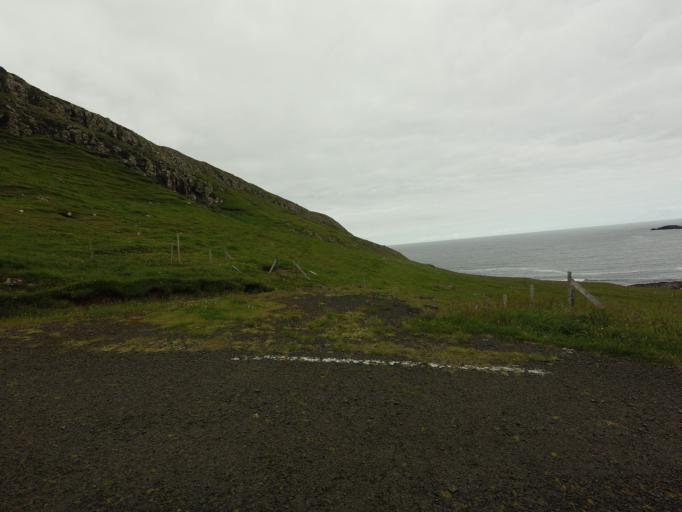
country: FO
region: Suduroy
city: Vagur
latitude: 61.4429
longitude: -6.7272
